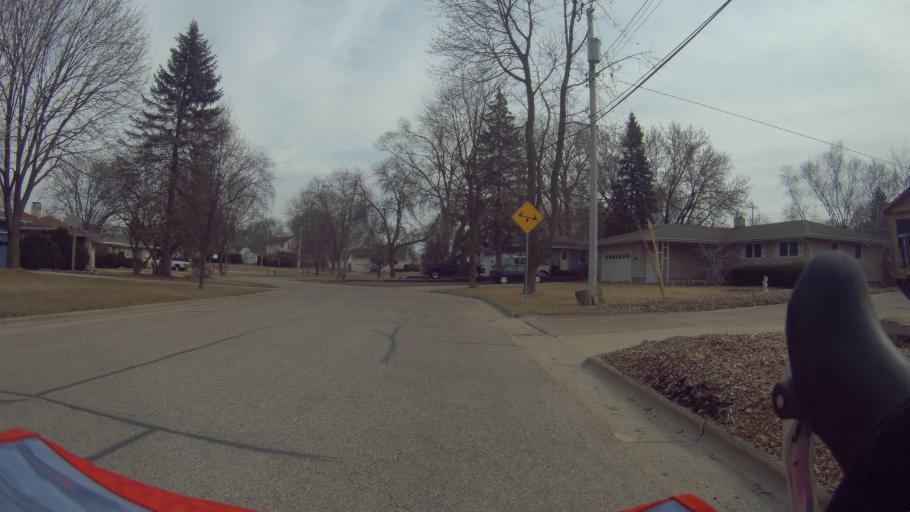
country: US
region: Wisconsin
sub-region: Dane County
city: Maple Bluff
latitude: 43.1201
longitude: -89.3692
